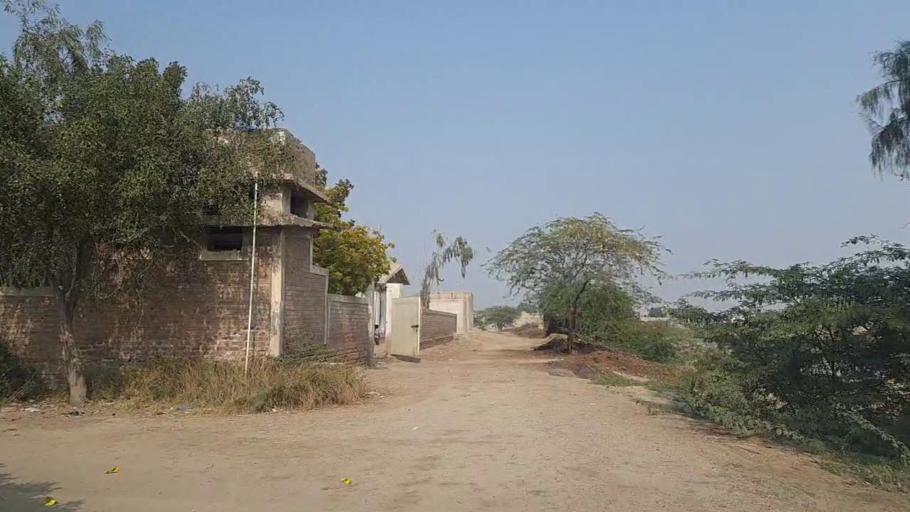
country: PK
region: Sindh
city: Daur
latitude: 26.4634
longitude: 68.4483
